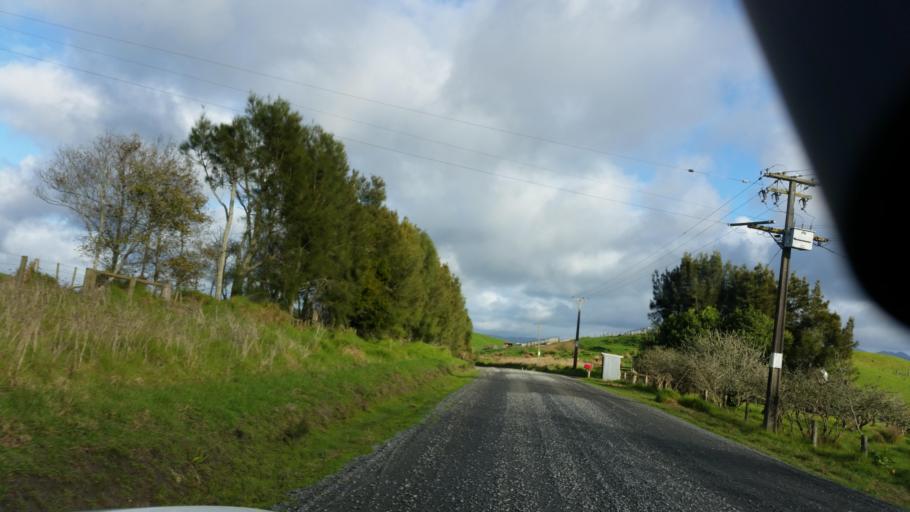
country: NZ
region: Northland
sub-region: Whangarei
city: Maungatapere
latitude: -35.7026
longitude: 174.0912
